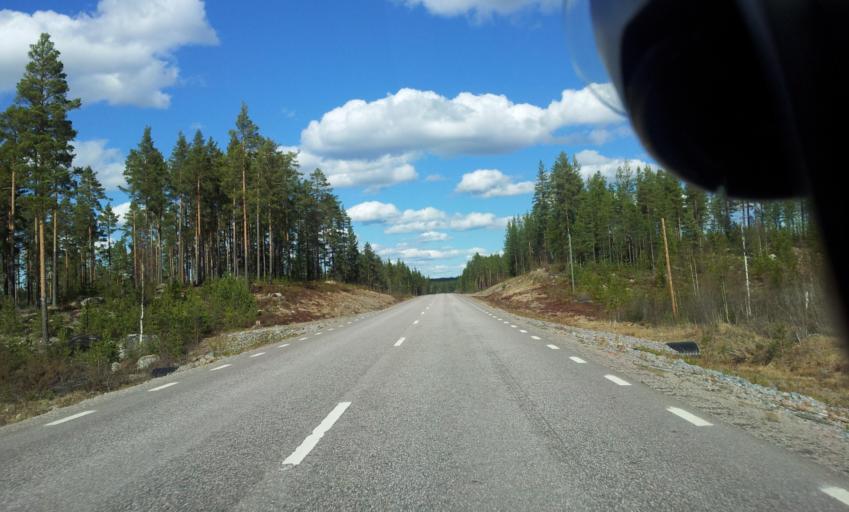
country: SE
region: Gaevleborg
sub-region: Ovanakers Kommun
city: Edsbyn
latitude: 61.2601
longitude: 15.8859
